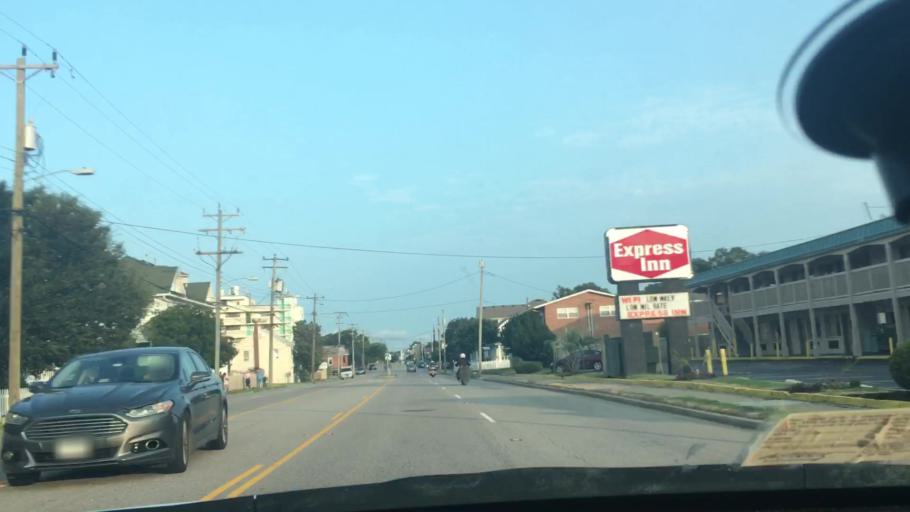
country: US
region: Virginia
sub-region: City of Norfolk
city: Norfolk
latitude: 36.9458
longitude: -76.2384
